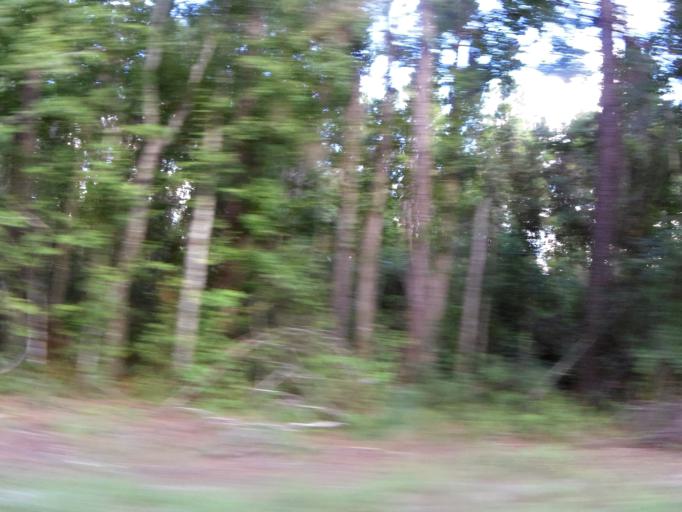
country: US
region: Georgia
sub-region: Camden County
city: Woodbine
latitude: 31.0430
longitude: -81.7298
